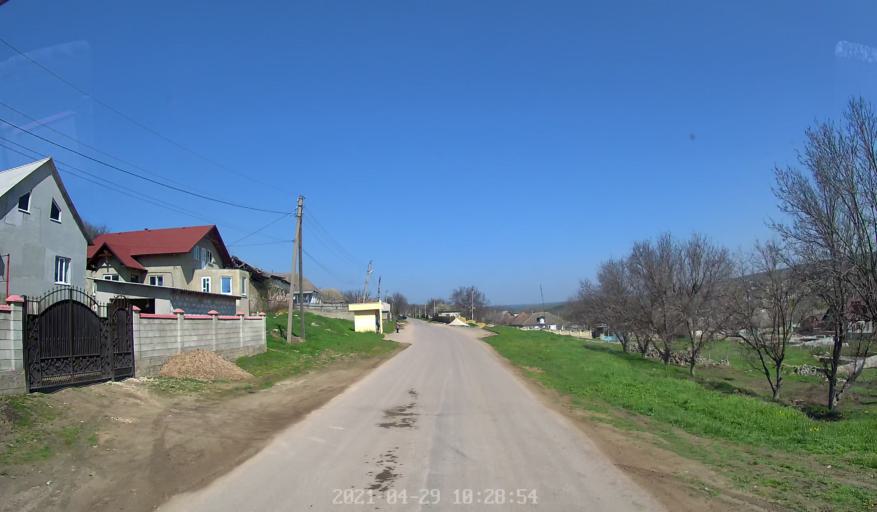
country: MD
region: Chisinau
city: Ciorescu
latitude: 47.1607
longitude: 28.9537
